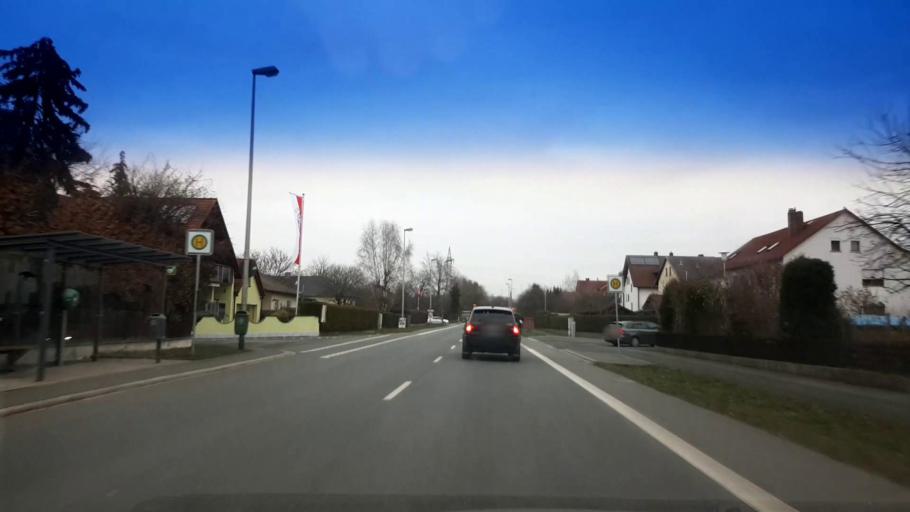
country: DE
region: Bavaria
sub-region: Upper Franconia
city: Altendorf
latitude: 49.8002
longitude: 11.0145
